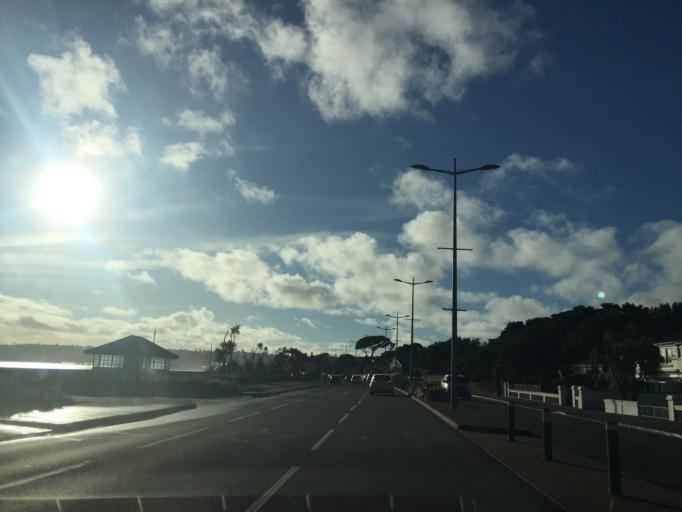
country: JE
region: St Helier
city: Saint Helier
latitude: 49.1962
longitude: -2.1358
